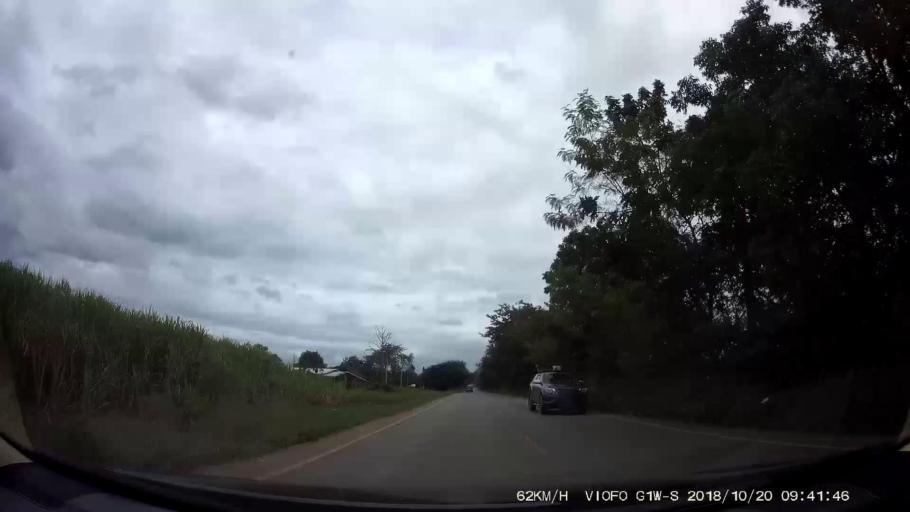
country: TH
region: Chaiyaphum
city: Khon San
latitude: 16.4565
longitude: 101.9556
